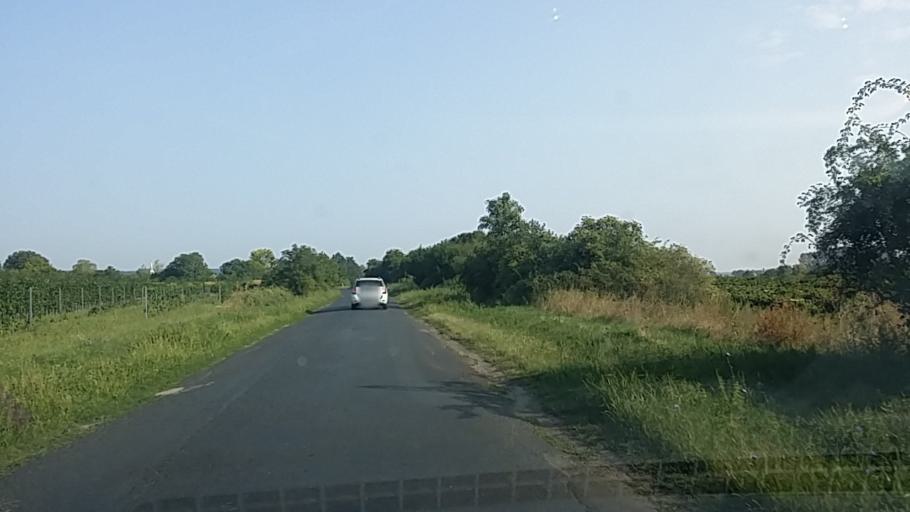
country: HU
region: Gyor-Moson-Sopron
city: Fertorakos
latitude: 47.7067
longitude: 16.6571
